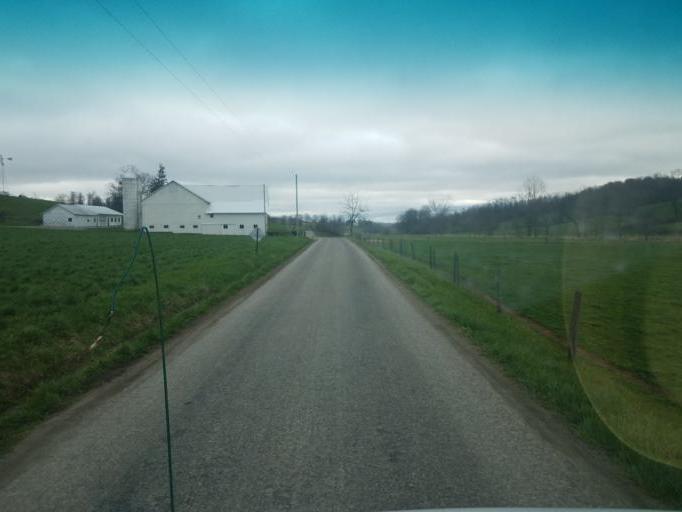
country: US
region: Ohio
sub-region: Stark County
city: Brewster
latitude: 40.6426
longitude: -81.7343
